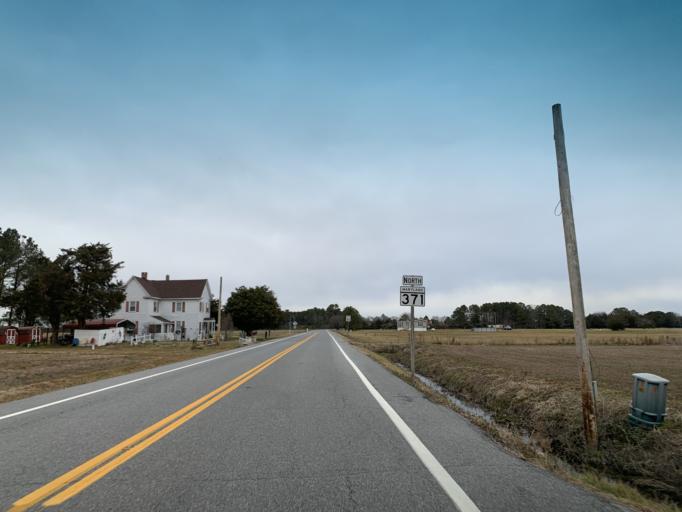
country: US
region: Maryland
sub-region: Worcester County
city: Pocomoke City
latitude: 38.0206
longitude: -75.6095
